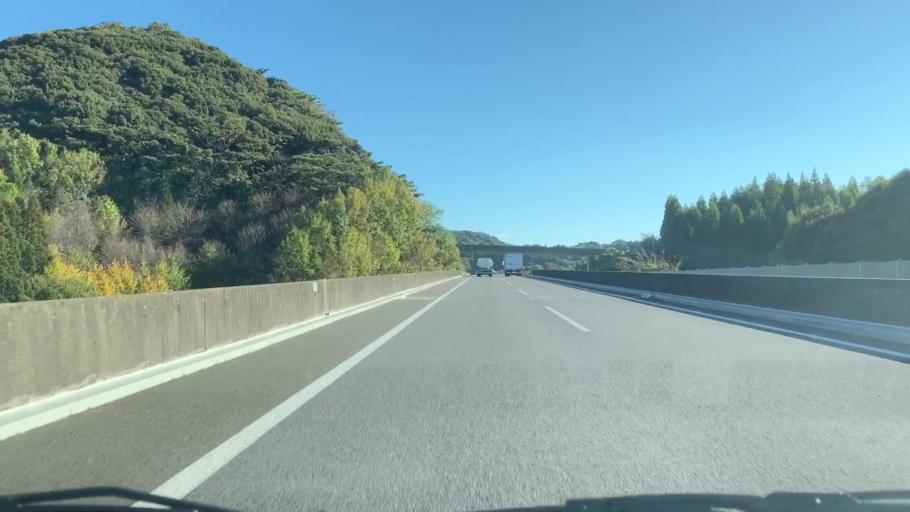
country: JP
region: Saga Prefecture
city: Saga-shi
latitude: 33.2995
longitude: 130.1813
